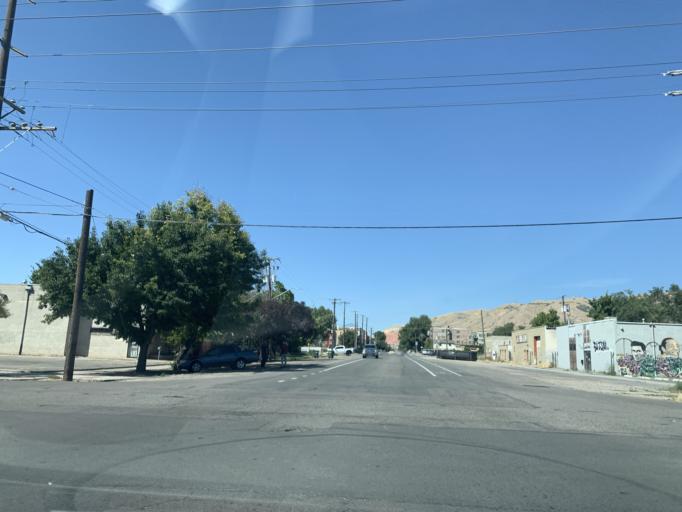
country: US
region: Utah
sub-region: Salt Lake County
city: Salt Lake City
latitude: 40.7671
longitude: -111.9082
